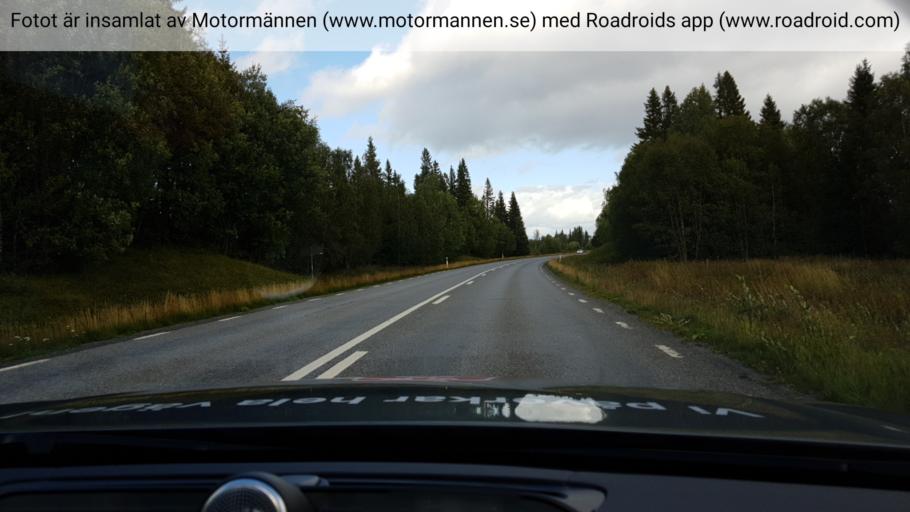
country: SE
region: Jaemtland
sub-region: OEstersunds Kommun
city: Lit
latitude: 63.4370
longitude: 15.1256
